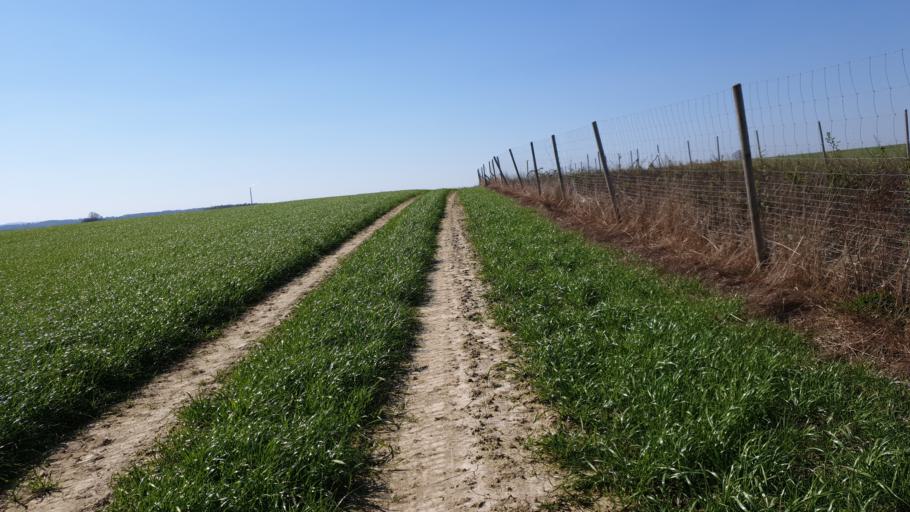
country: DE
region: Saxony
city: Claussnitz
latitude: 50.9276
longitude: 12.9120
